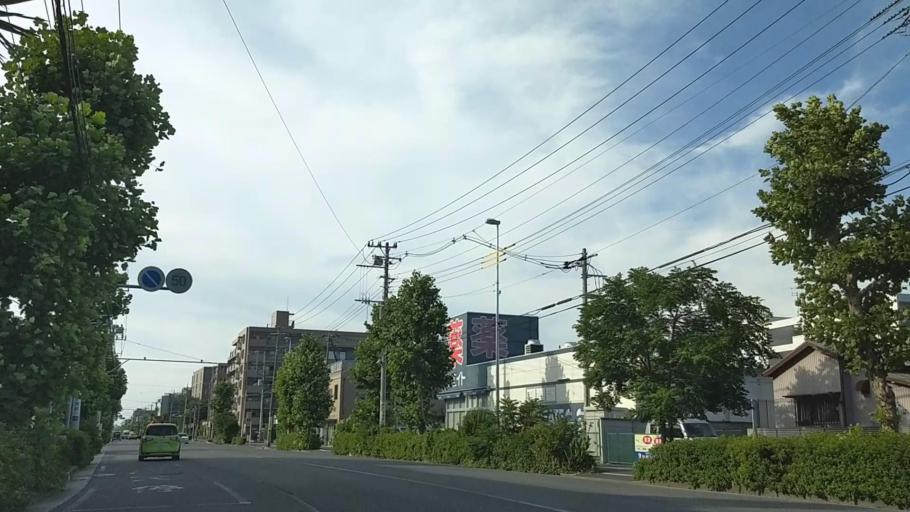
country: JP
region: Kanagawa
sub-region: Kawasaki-shi
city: Kawasaki
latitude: 35.5032
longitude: 139.6940
